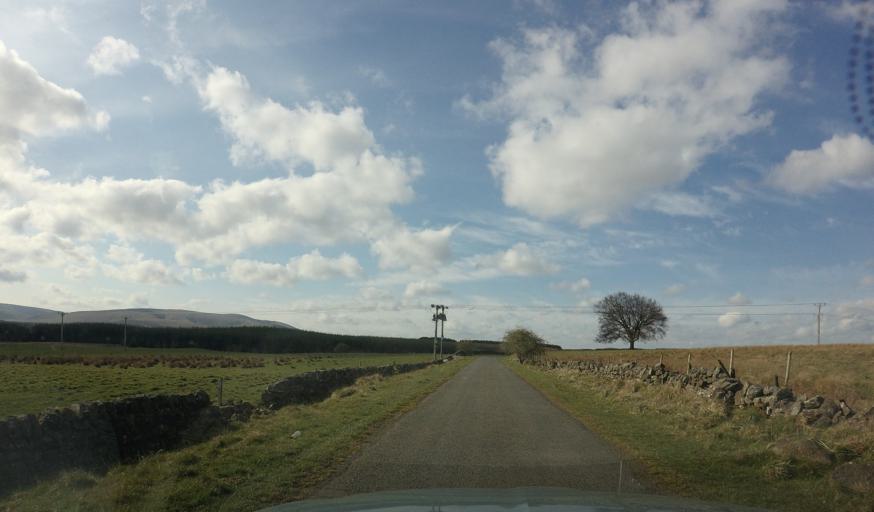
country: GB
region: Scotland
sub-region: Midlothian
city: Penicuik
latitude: 55.7894
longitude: -3.1682
